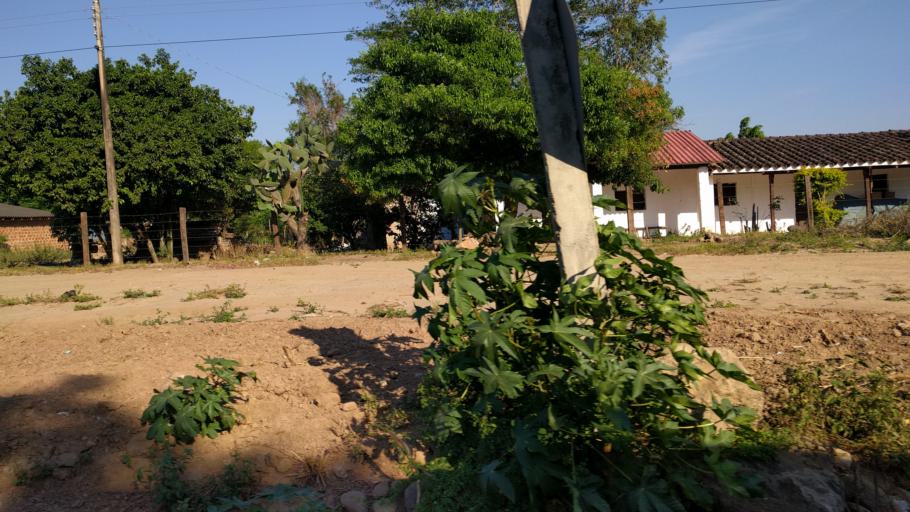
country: BO
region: Santa Cruz
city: Jorochito
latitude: -18.1437
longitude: -63.4815
